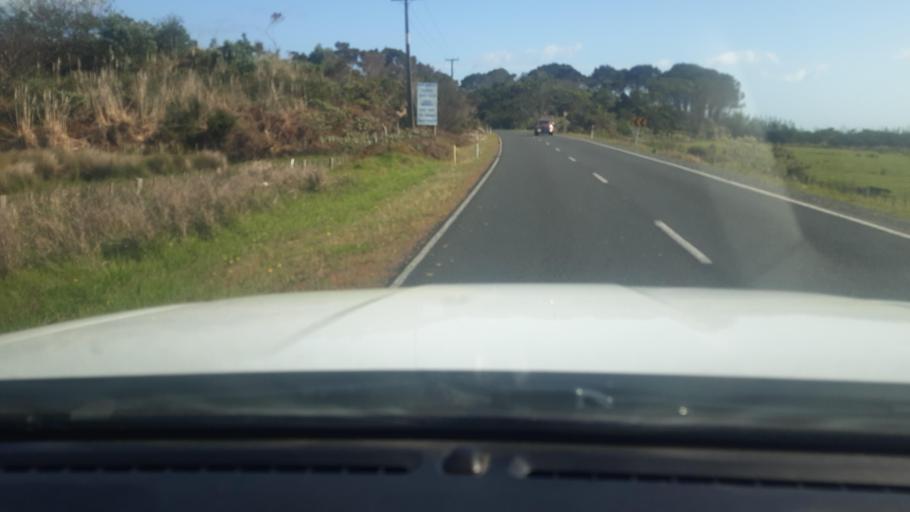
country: NZ
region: Northland
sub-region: Far North District
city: Taipa
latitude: -34.9018
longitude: 173.3504
